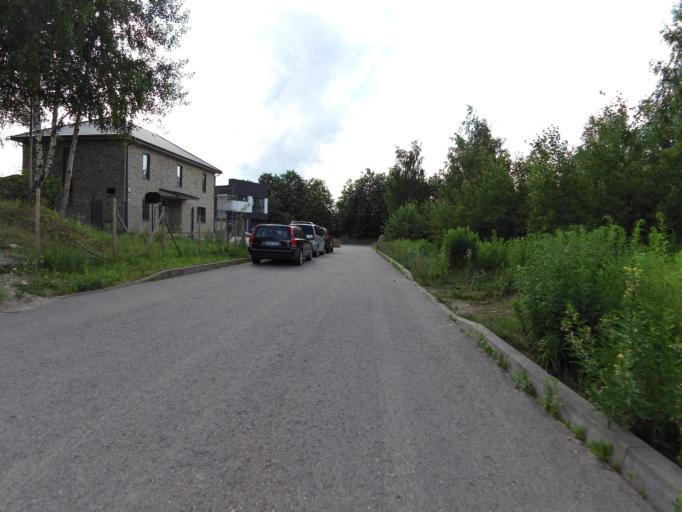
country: LT
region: Vilnius County
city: Pasilaiciai
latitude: 54.7633
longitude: 25.2271
